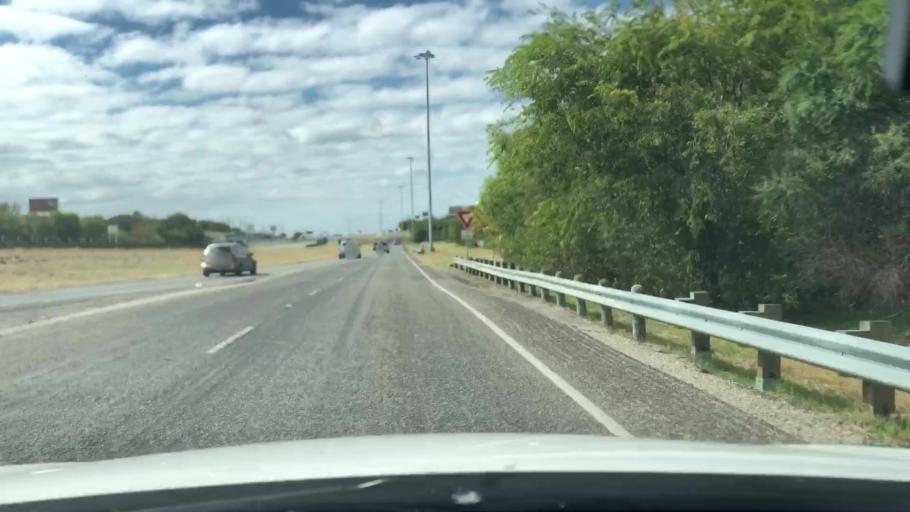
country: US
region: Texas
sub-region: Bexar County
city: Lackland Air Force Base
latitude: 29.4063
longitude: -98.6102
